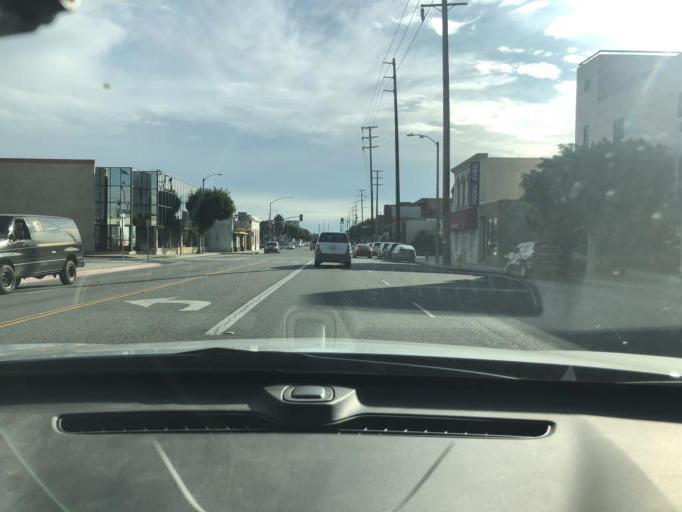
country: US
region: California
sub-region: Los Angeles County
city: Gardena
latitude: 33.8810
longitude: -118.3092
